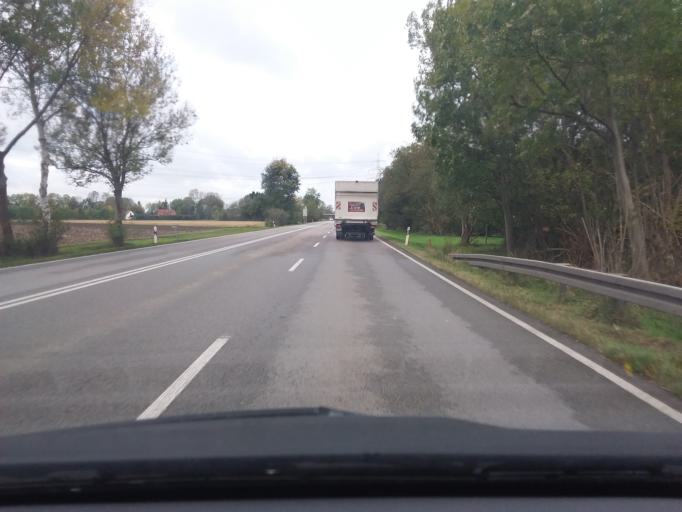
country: DE
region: Bavaria
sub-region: Upper Bavaria
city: Dachau
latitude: 48.2346
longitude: 11.4014
